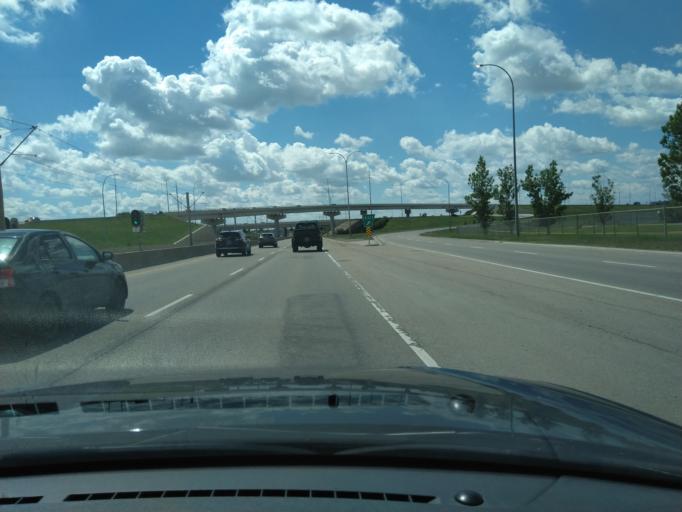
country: CA
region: Alberta
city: Calgary
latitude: 51.0990
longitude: -113.9820
